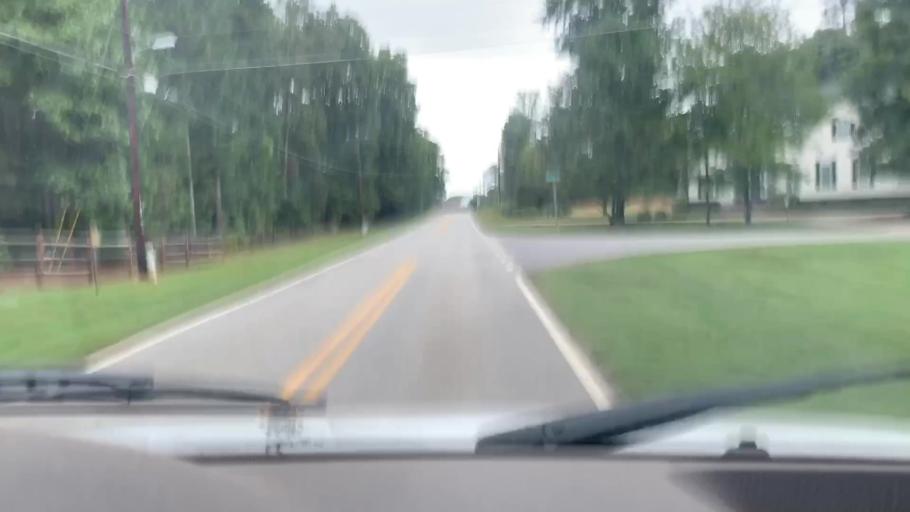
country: US
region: North Carolina
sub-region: Catawba County
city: Lake Norman of Catawba
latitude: 35.5509
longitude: -80.9062
